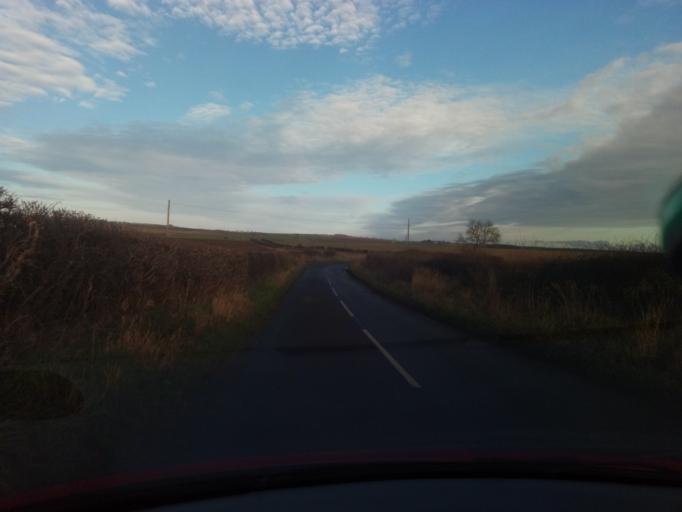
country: GB
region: Scotland
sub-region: The Scottish Borders
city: Chirnside
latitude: 55.8458
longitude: -2.1883
